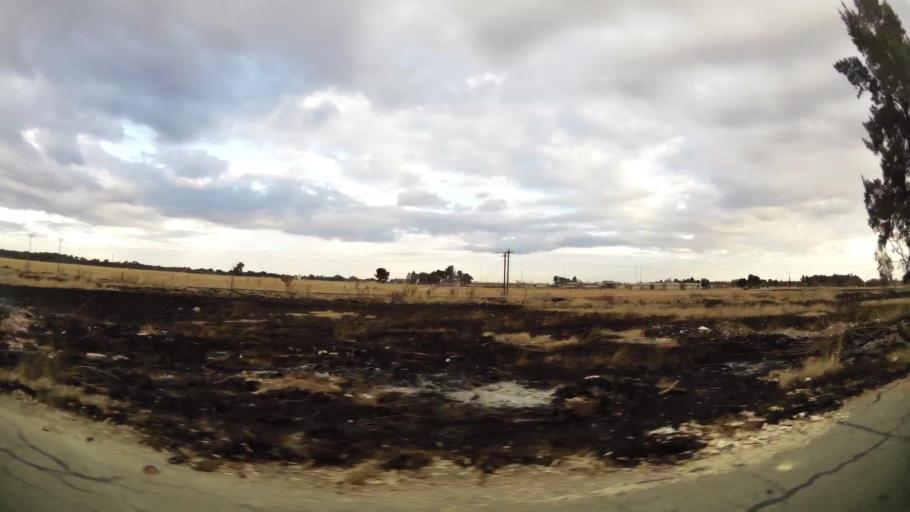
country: ZA
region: Orange Free State
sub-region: Lejweleputswa District Municipality
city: Welkom
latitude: -27.9642
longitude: 26.7051
